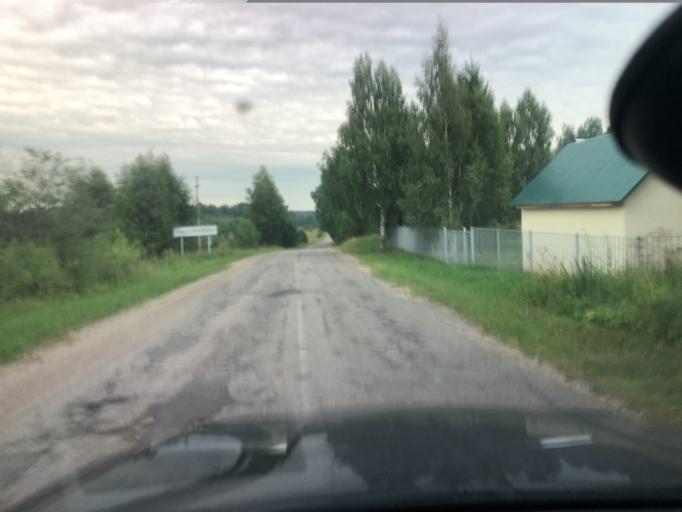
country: RU
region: Jaroslavl
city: Petrovsk
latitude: 57.0106
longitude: 38.9796
